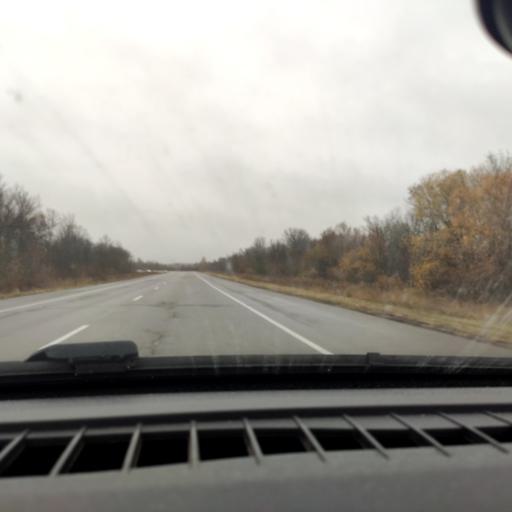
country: RU
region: Voronezj
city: Kolodeznyy
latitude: 51.3019
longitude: 39.0395
